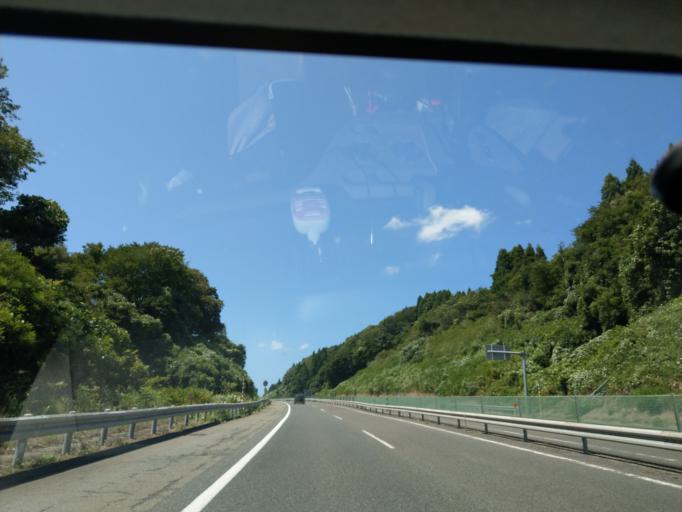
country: JP
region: Akita
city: Akita
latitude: 39.6543
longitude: 140.2018
